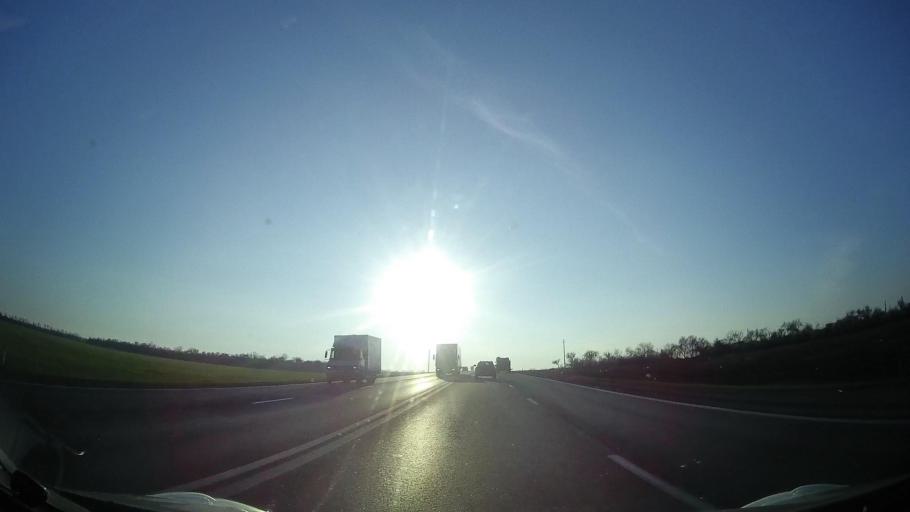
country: RU
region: Rostov
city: Bataysk
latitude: 47.0911
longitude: 39.7961
